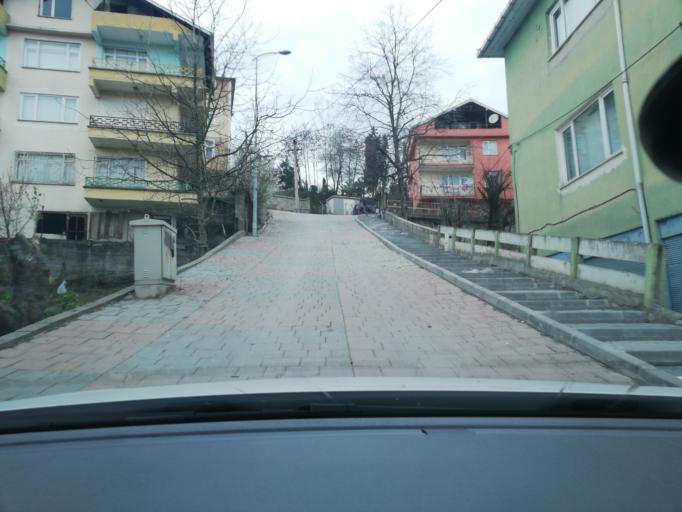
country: TR
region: Zonguldak
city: Gokcebey
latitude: 41.3084
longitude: 32.1393
